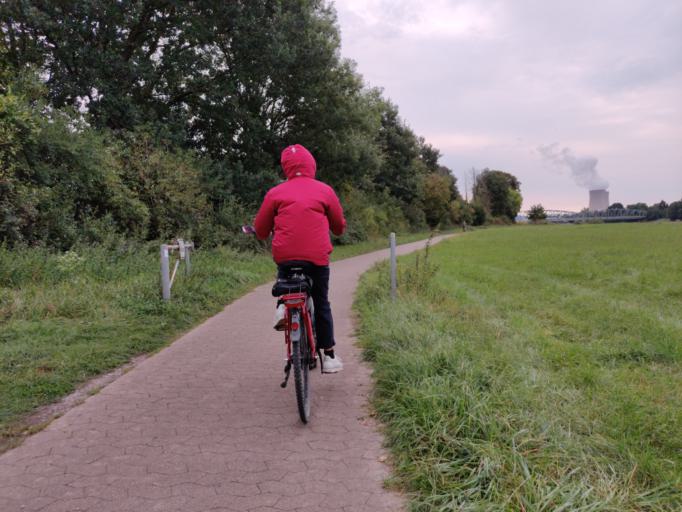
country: DE
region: Lower Saxony
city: Hameln
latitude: 52.0532
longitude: 9.3896
